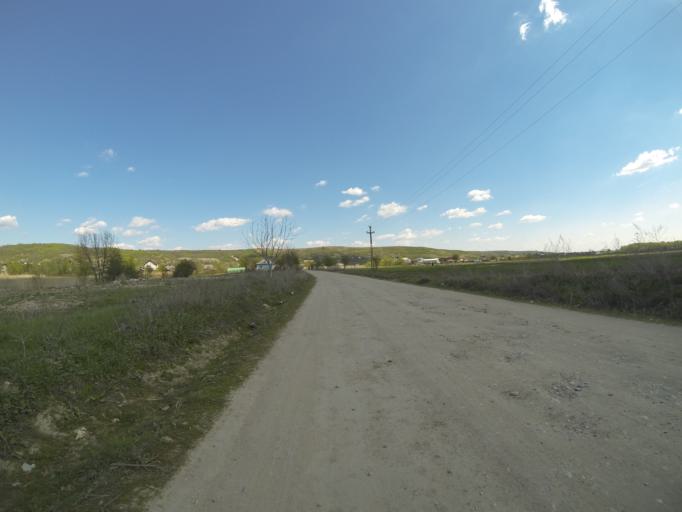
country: RO
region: Dolj
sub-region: Comuna Goesti
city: Goesti
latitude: 44.4992
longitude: 23.7491
